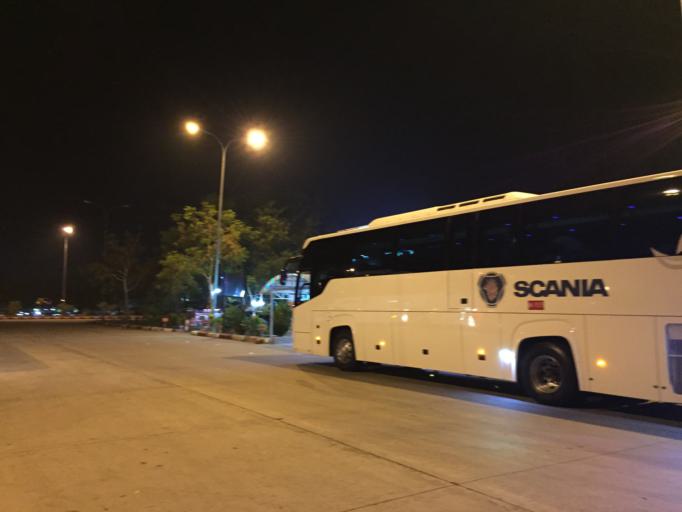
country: MM
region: Mandalay
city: Nay Pyi Taw
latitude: 19.6601
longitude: 96.0581
